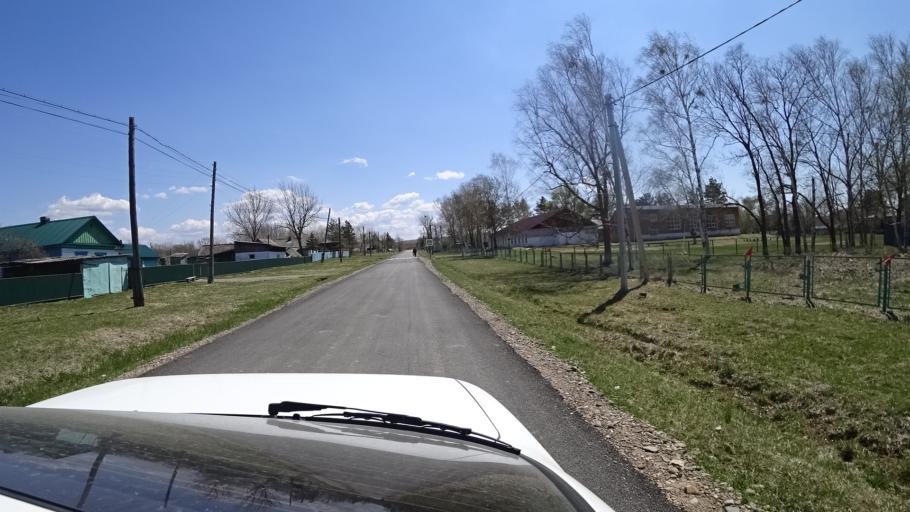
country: RU
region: Primorskiy
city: Dal'nerechensk
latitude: 45.7957
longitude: 133.7681
